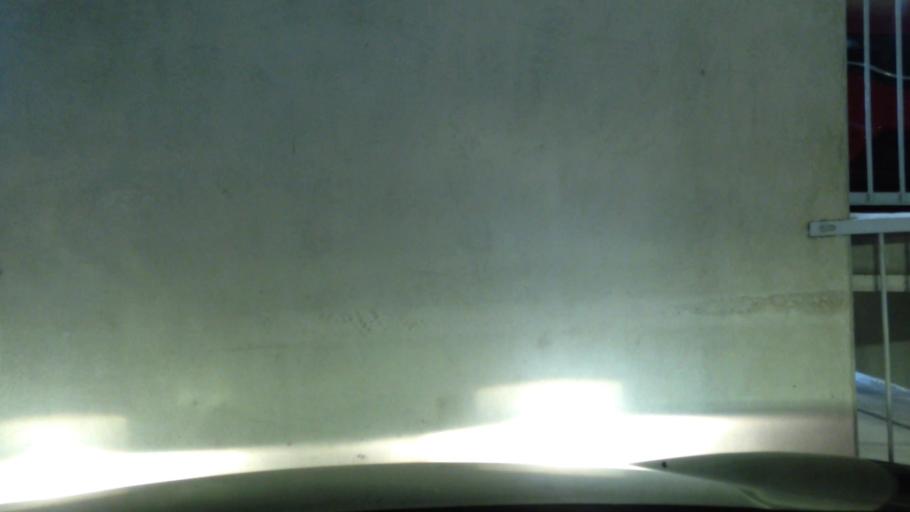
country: US
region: Texas
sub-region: Bexar County
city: Balcones Heights
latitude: 29.5191
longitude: -98.5763
